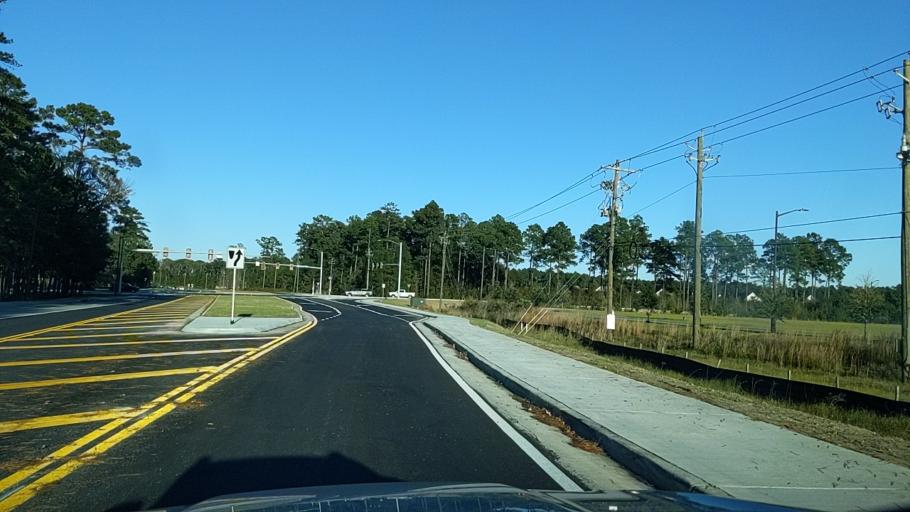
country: US
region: Georgia
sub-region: Chatham County
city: Pooler
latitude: 32.1769
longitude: -81.2296
